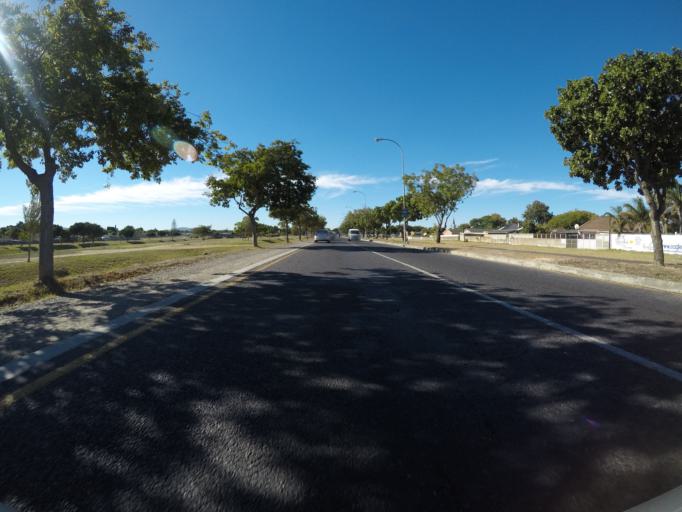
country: ZA
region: Western Cape
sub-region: City of Cape Town
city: Kraaifontein
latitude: -33.9290
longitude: 18.6767
